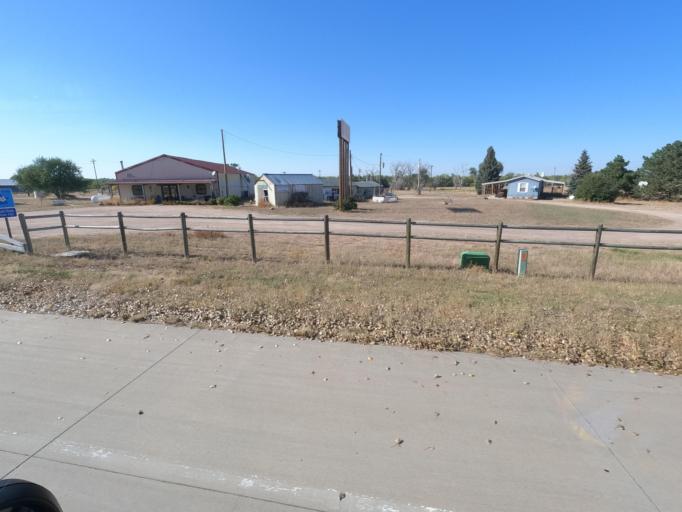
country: US
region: Colorado
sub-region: Sedgwick County
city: Julesburg
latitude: 40.9668
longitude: -102.2517
